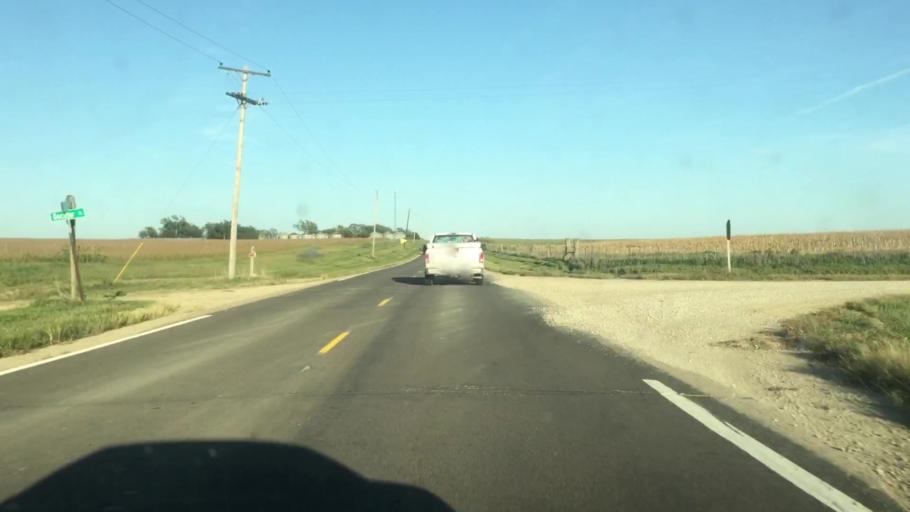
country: US
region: Kansas
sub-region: Brown County
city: Horton
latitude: 39.5515
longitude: -95.4400
